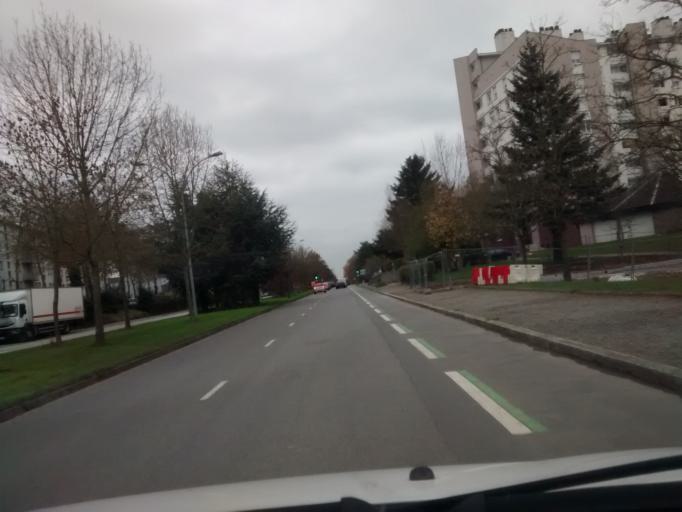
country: FR
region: Brittany
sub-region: Departement d'Ille-et-Vilaine
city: Rennes
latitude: 48.1278
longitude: -1.6553
